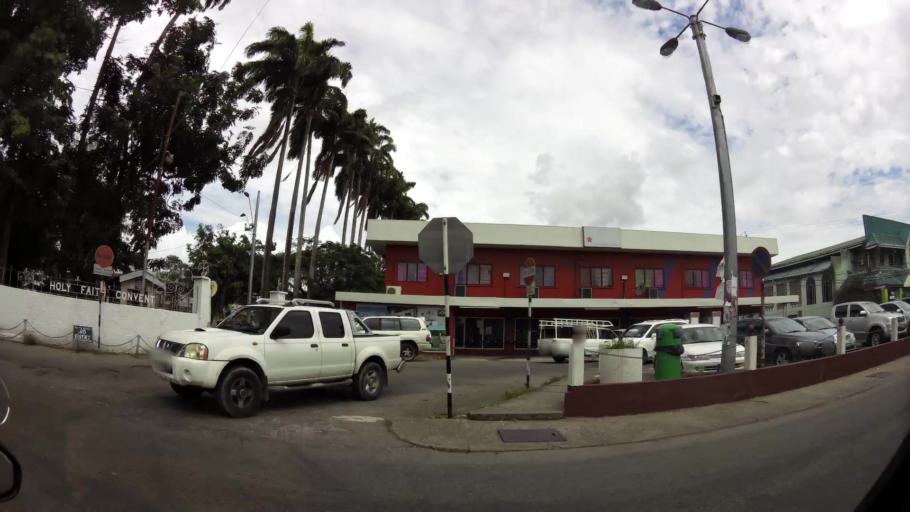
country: TT
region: Couva-Tabaquite-Talparo
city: Couva
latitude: 10.4220
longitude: -61.4616
